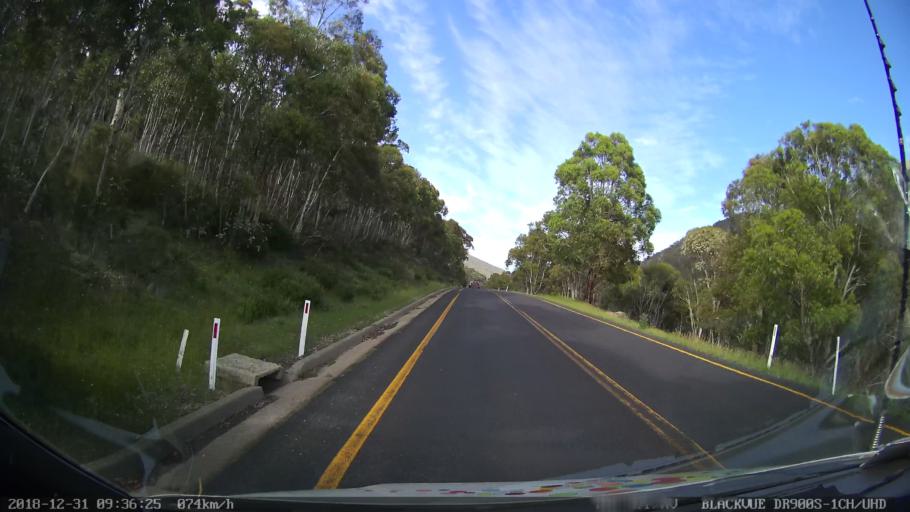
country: AU
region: New South Wales
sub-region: Snowy River
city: Jindabyne
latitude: -36.4585
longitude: 148.3867
